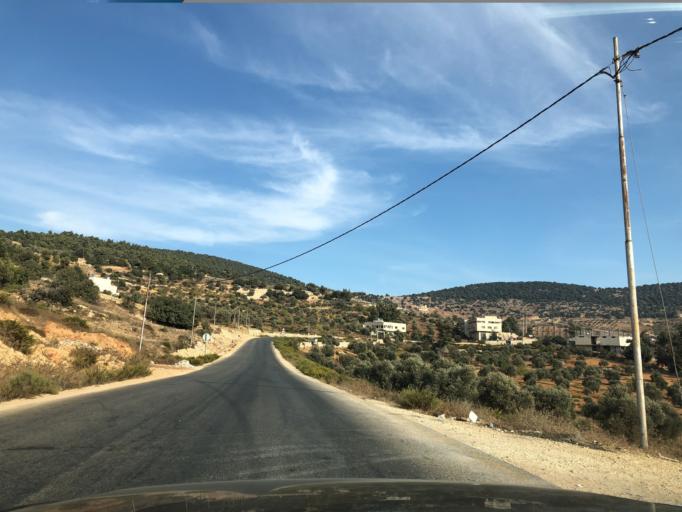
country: JO
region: Irbid
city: `Anjarah
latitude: 32.3170
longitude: 35.7687
